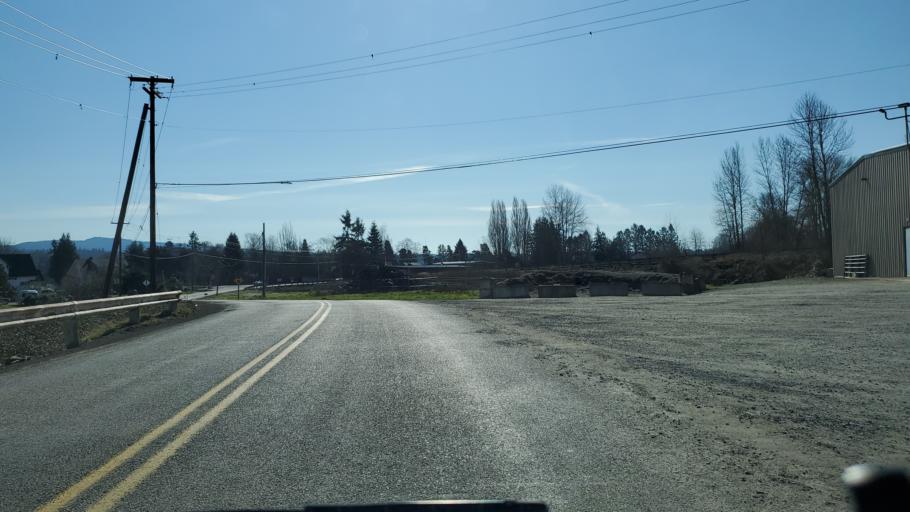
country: US
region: Washington
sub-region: Skagit County
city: Mount Vernon
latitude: 48.3426
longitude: -122.3488
